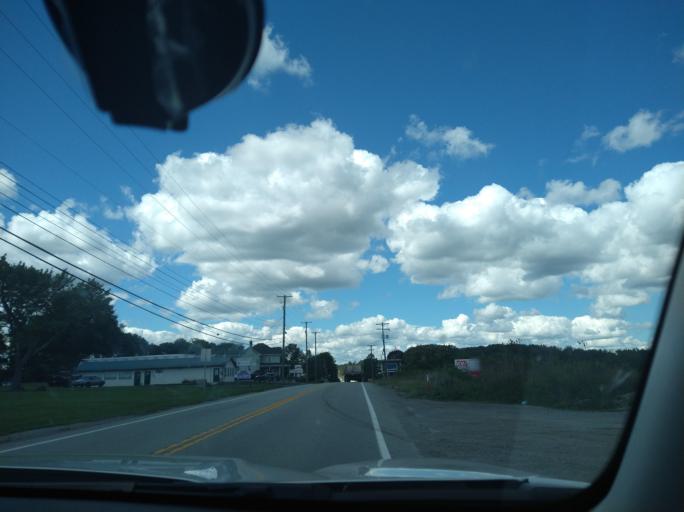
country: US
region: Pennsylvania
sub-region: Fayette County
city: Bear Rocks
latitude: 40.1046
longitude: -79.3716
